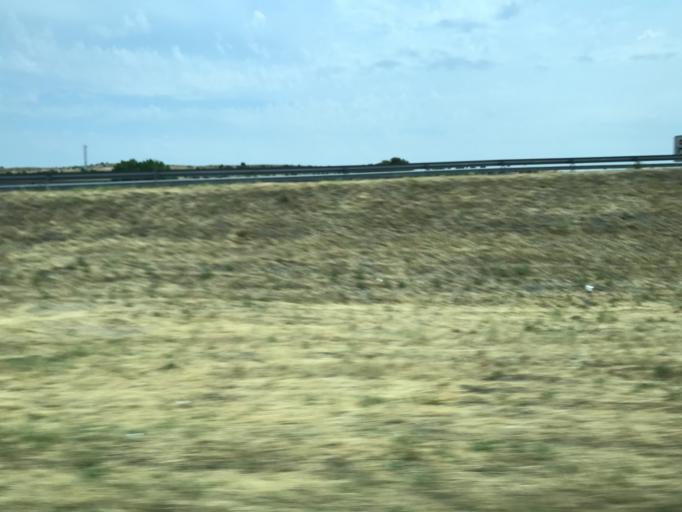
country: ES
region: Madrid
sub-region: Provincia de Madrid
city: San Agustin de Guadalix
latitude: 40.6458
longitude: -3.5952
